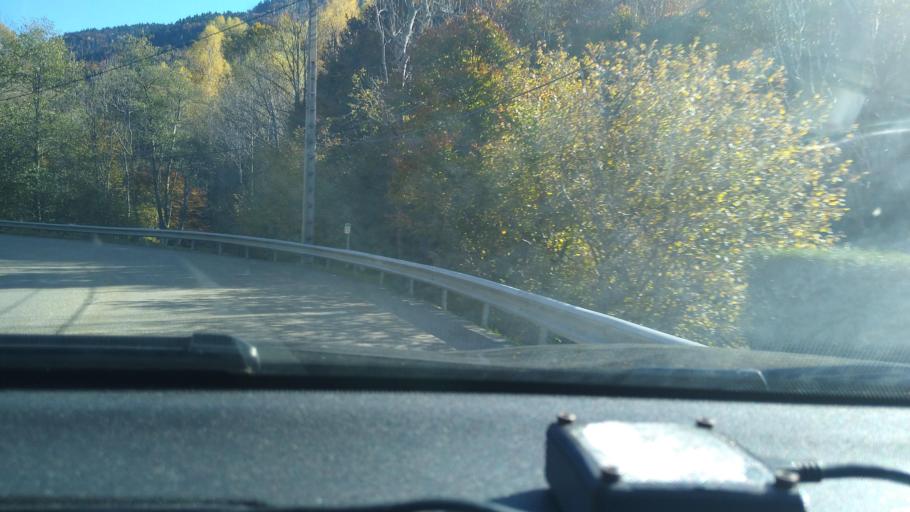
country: FR
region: Midi-Pyrenees
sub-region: Departement de l'Ariege
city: Ax-les-Thermes
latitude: 42.7216
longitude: 1.9022
